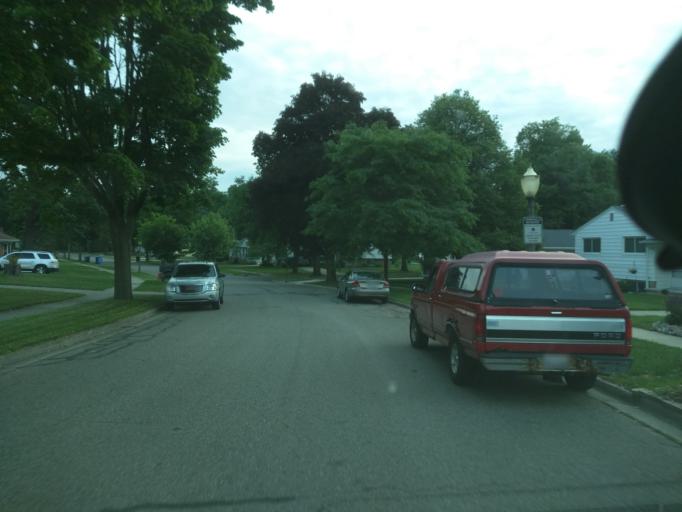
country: US
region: Michigan
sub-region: Ingham County
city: Lansing
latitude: 42.7034
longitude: -84.5745
